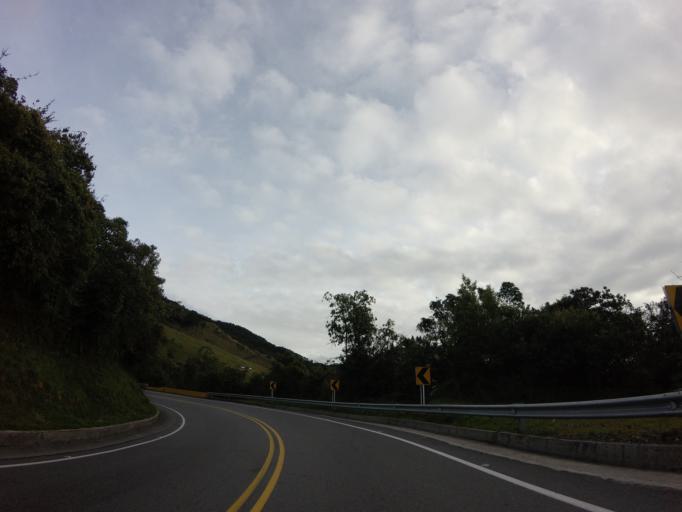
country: CO
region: Tolima
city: Herveo
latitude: 5.1015
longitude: -75.2769
